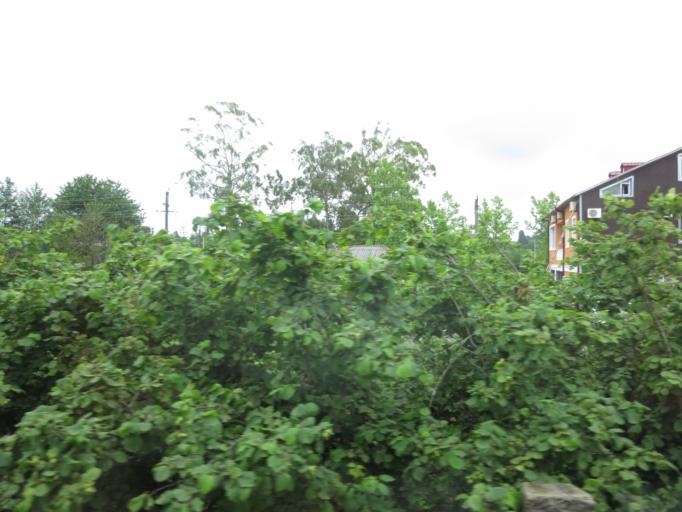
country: GE
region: Guria
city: Urek'i
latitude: 42.0075
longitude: 41.7799
